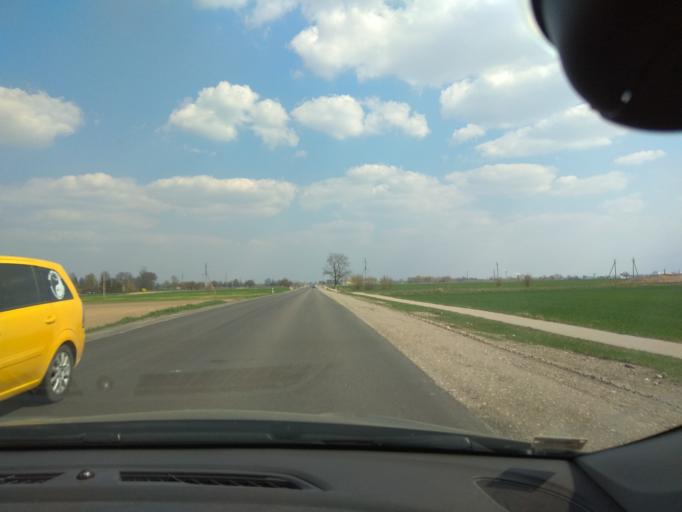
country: LT
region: Kauno apskritis
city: Kedainiai
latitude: 55.2674
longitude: 23.9128
